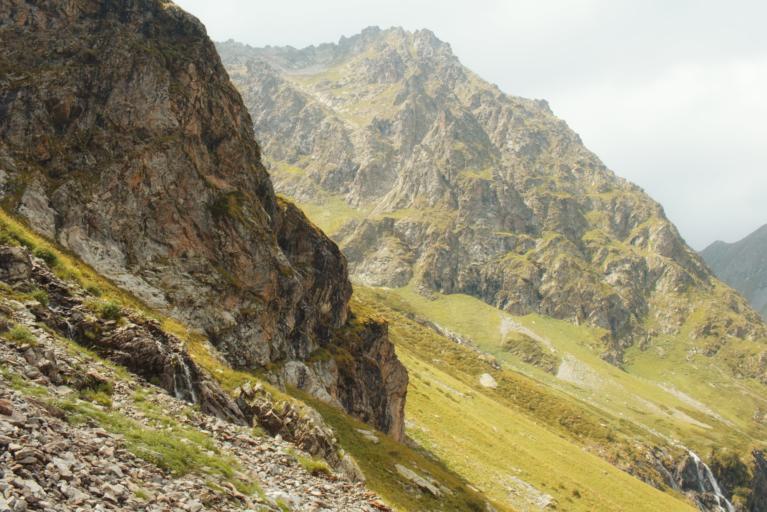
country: RU
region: Karachayevo-Cherkesiya
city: Nizhniy Arkhyz
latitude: 43.4389
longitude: 41.2556
